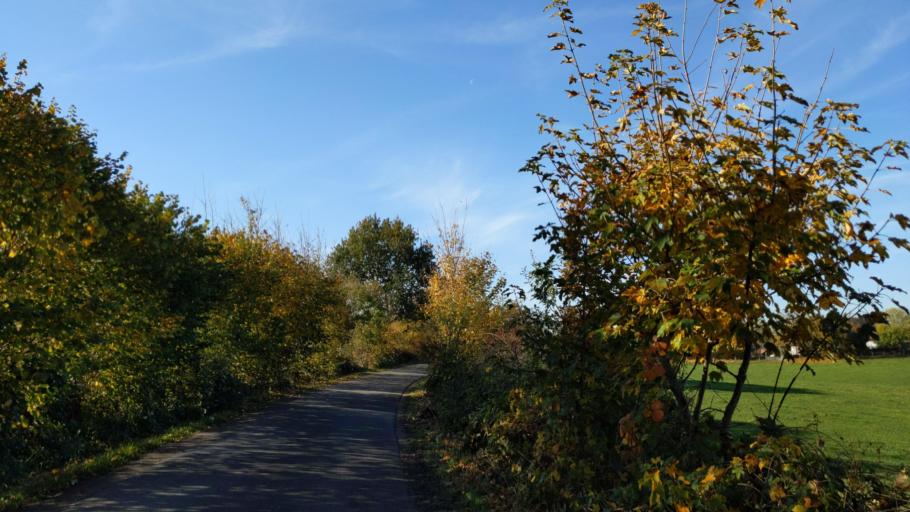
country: DE
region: Schleswig-Holstein
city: Kasseedorf
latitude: 54.1305
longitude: 10.7434
